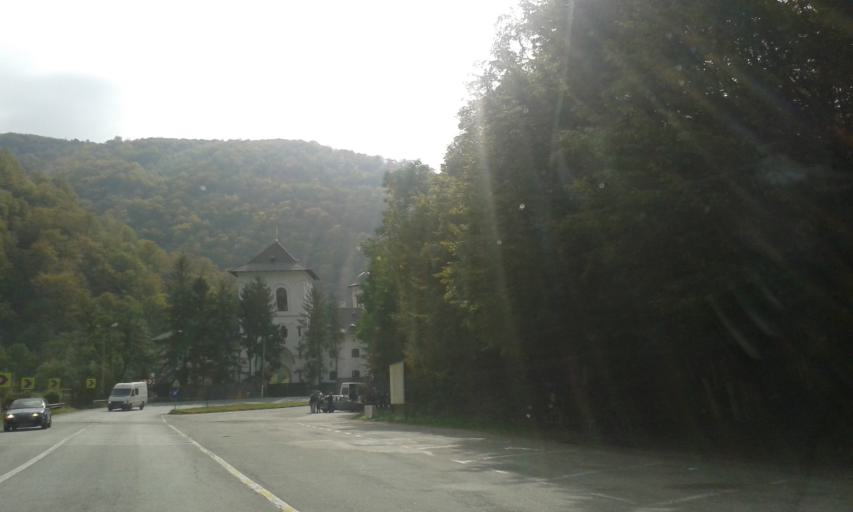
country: RO
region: Gorj
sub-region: Comuna Bumbesti-Jiu
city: Bumbesti-Jiu
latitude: 45.2657
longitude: 23.3926
